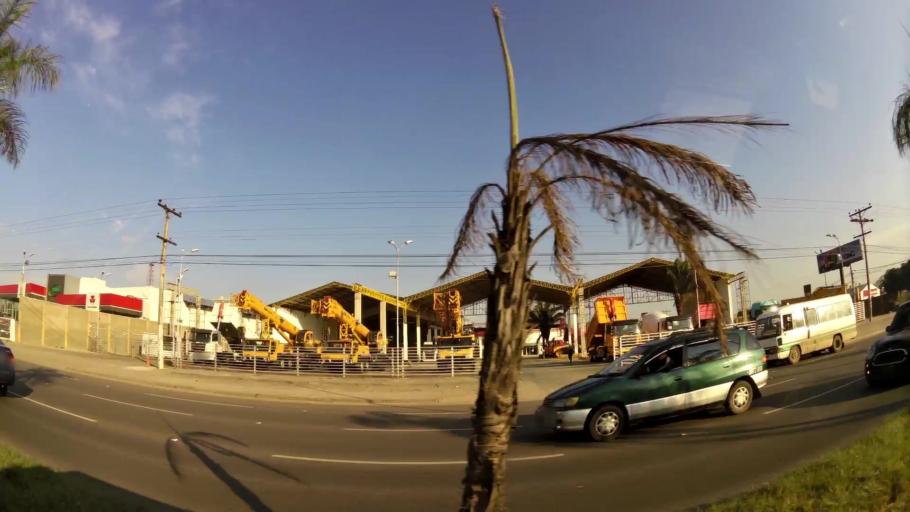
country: BO
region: Santa Cruz
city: Santa Cruz de la Sierra
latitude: -17.7192
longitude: -63.1632
